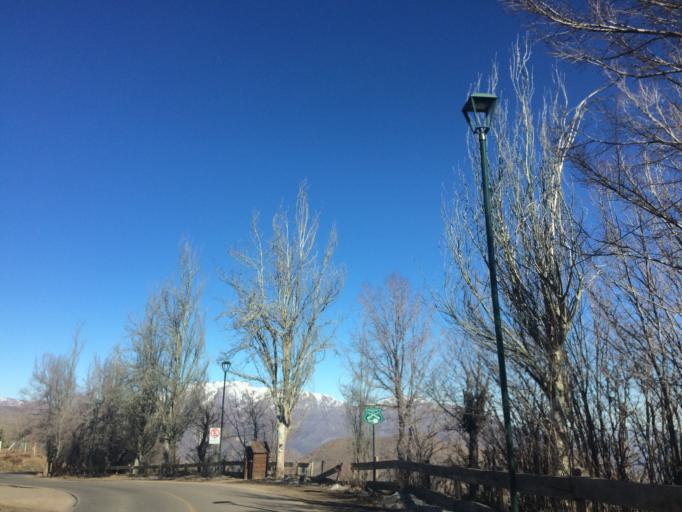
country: CL
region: Santiago Metropolitan
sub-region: Provincia de Santiago
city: Villa Presidente Frei, Nunoa, Santiago, Chile
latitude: -33.3517
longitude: -70.3159
